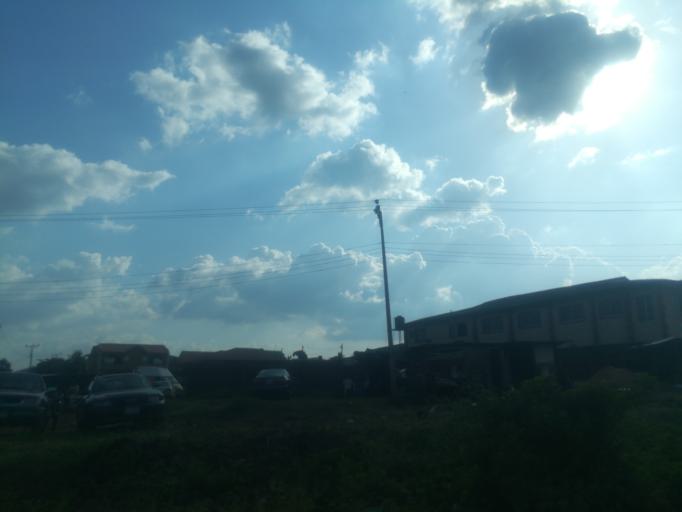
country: NG
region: Oyo
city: Ibadan
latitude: 7.3887
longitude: 3.9779
